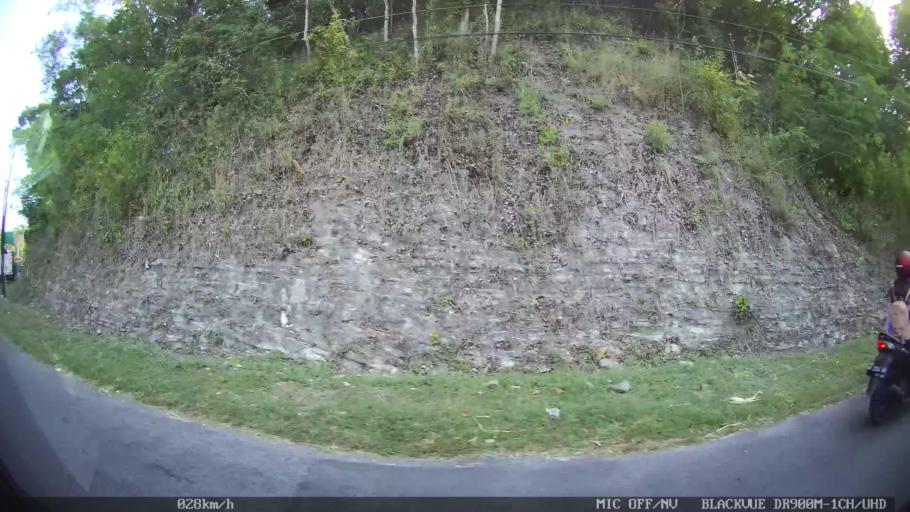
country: ID
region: Daerah Istimewa Yogyakarta
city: Bantul
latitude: -7.8751
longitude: 110.3150
